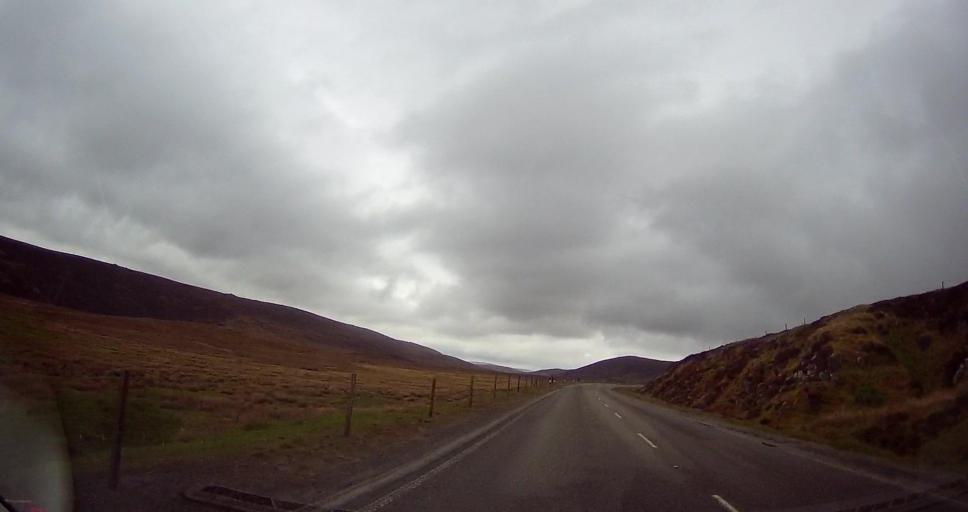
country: GB
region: Scotland
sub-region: Shetland Islands
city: Lerwick
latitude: 60.2871
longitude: -1.2411
